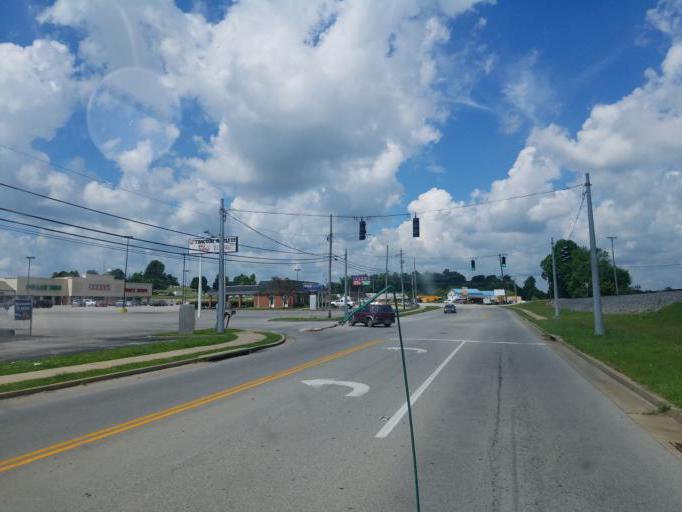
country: US
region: Kentucky
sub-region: Grayson County
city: Leitchfield
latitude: 37.4857
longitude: -86.2734
